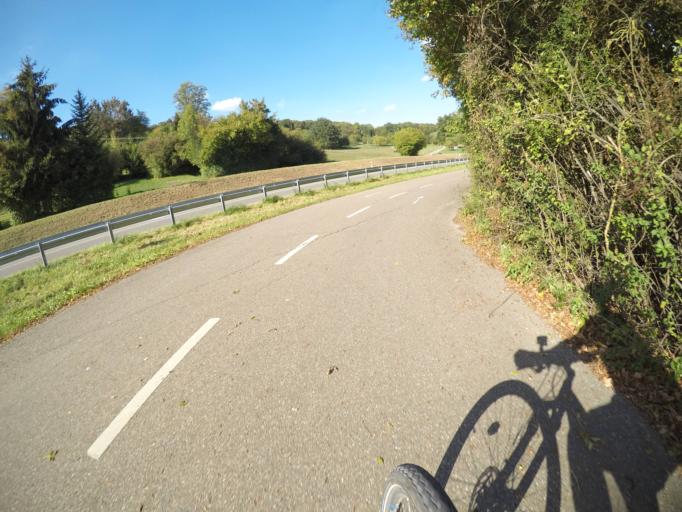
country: DE
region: Baden-Wuerttemberg
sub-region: Regierungsbezirk Stuttgart
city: Denkendorf
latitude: 48.6973
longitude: 9.3348
